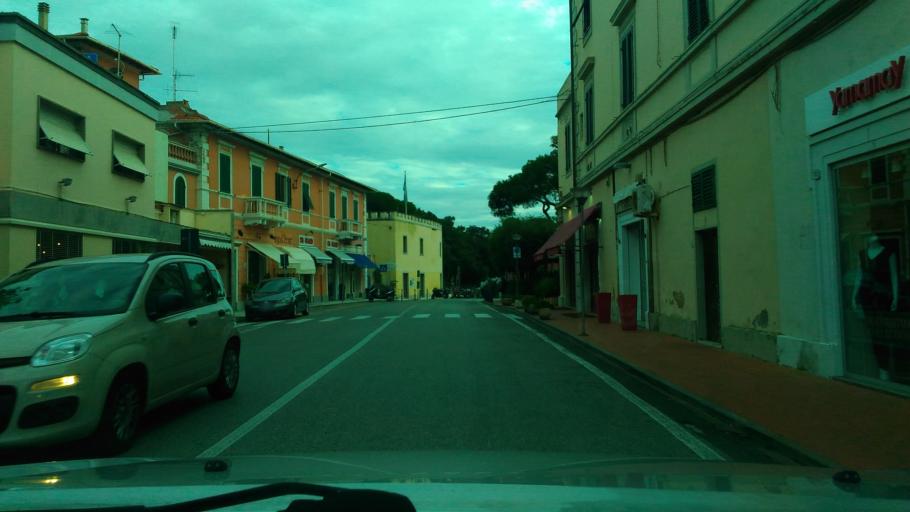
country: IT
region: Tuscany
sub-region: Provincia di Livorno
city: Rosignano Solvay-Castiglioncello
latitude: 43.4059
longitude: 10.4095
